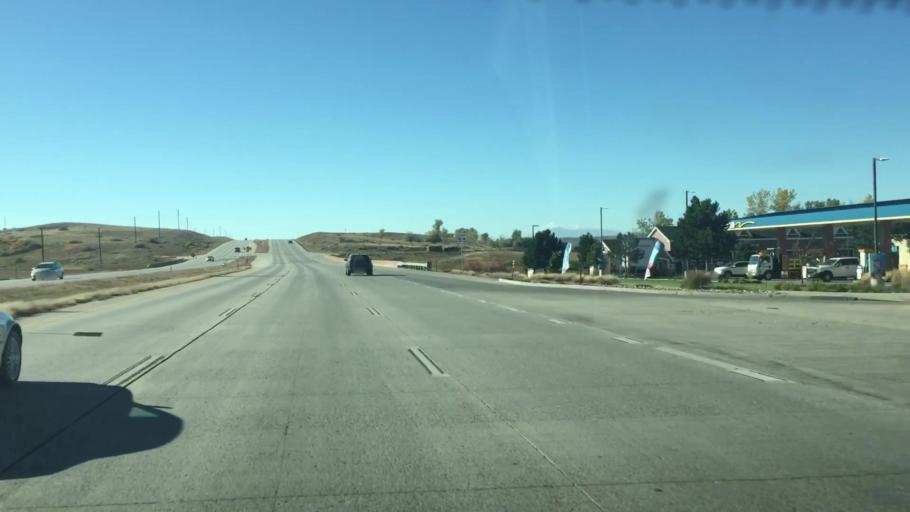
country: US
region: Colorado
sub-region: Douglas County
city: The Pinery
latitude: 39.4767
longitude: -104.7583
